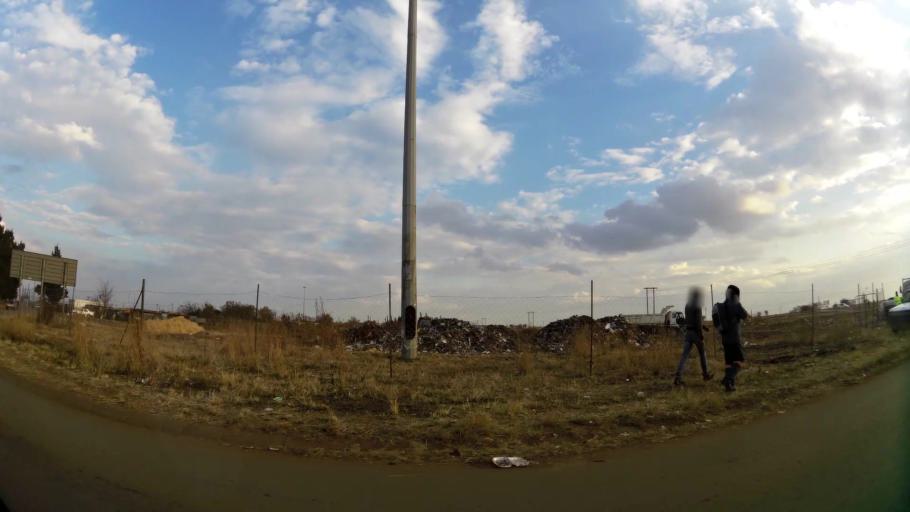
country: ZA
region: Gauteng
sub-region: City of Johannesburg Metropolitan Municipality
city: Orange Farm
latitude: -26.5909
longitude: 27.8224
